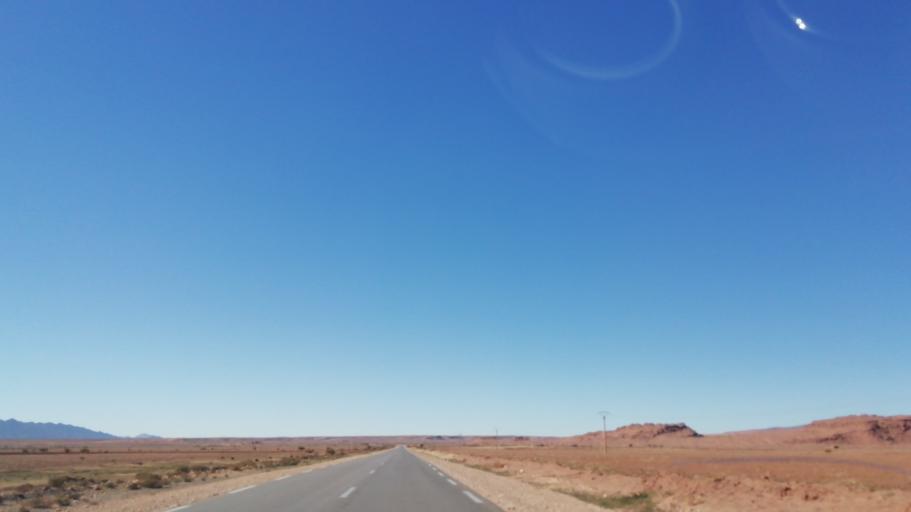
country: DZ
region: El Bayadh
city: El Abiodh Sidi Cheikh
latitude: 33.1776
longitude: 0.5356
